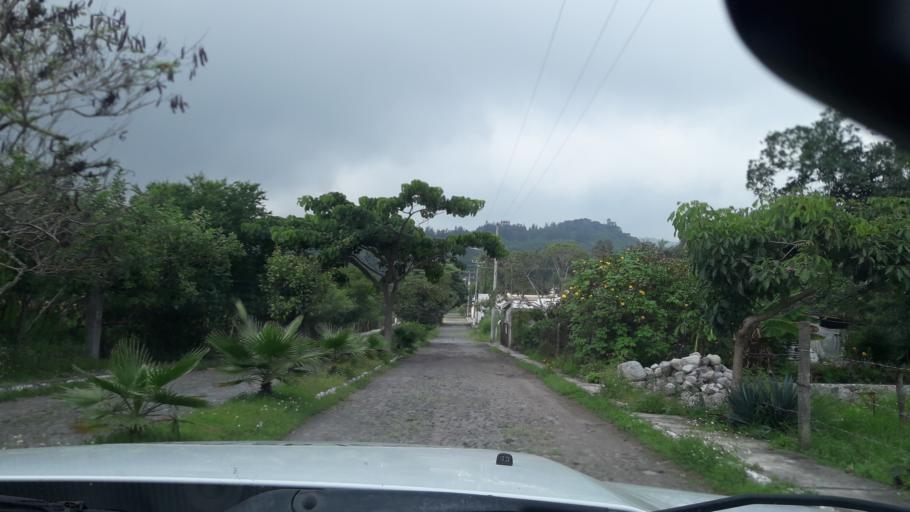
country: MX
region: Colima
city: Suchitlan
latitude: 19.4103
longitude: -103.6553
